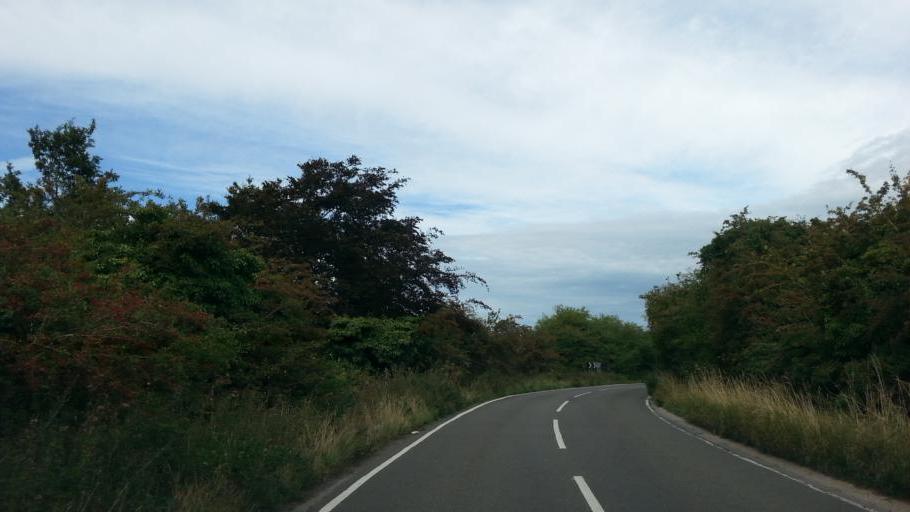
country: GB
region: England
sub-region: Cambridgeshire
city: Cambridge
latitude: 52.1766
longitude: 0.1646
